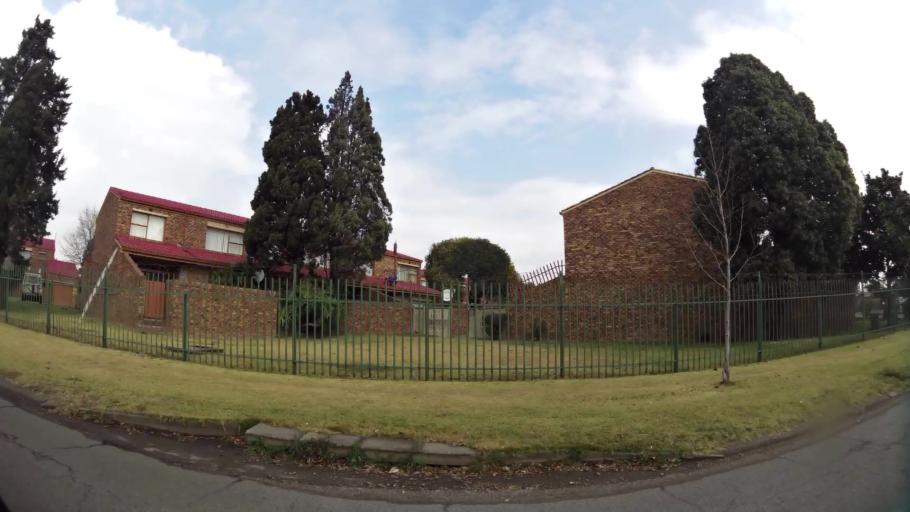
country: ZA
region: Gauteng
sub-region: Sedibeng District Municipality
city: Vanderbijlpark
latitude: -26.6923
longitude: 27.8494
